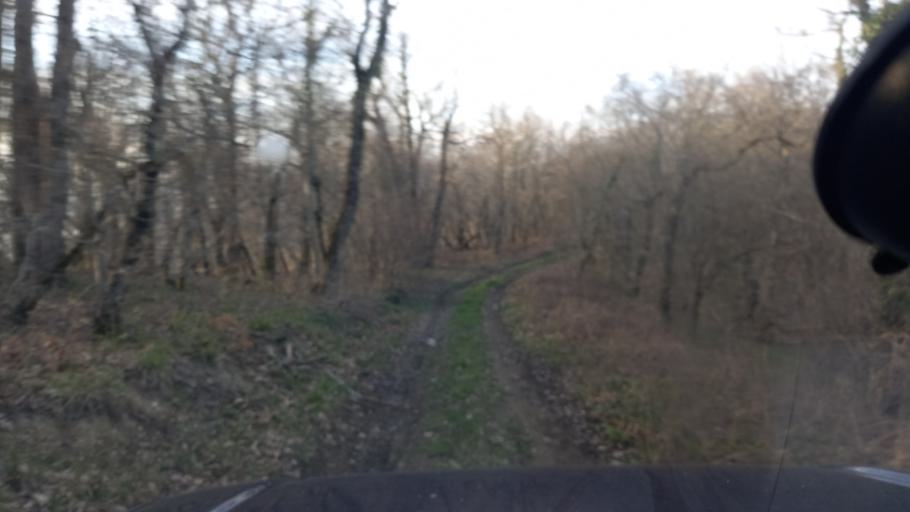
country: RU
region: Krasnodarskiy
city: Arkhipo-Osipovka
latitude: 44.3580
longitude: 38.5525
